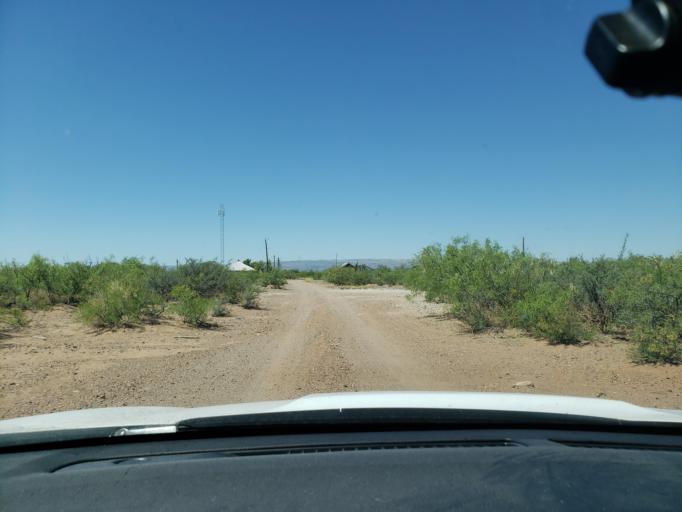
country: US
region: Texas
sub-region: Presidio County
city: Marfa
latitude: 30.5860
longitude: -104.4898
